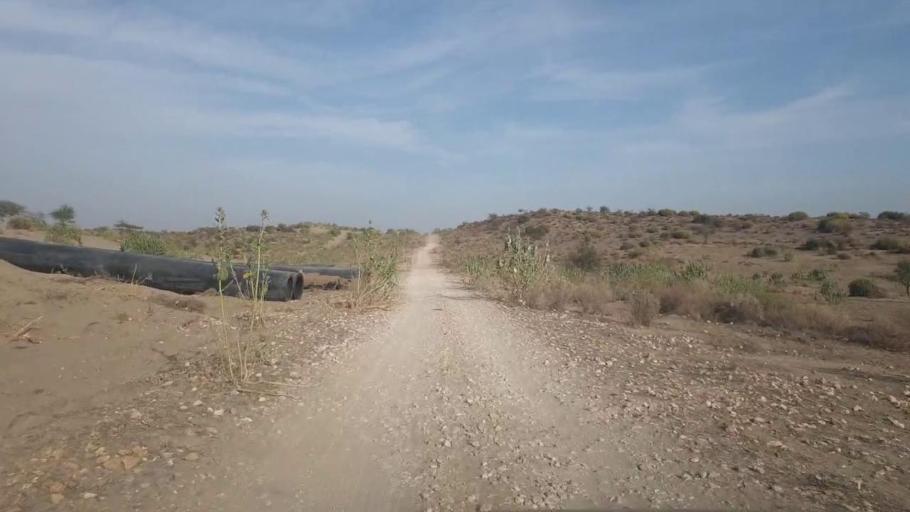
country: PK
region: Sindh
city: Nabisar
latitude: 25.0523
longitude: 69.7258
